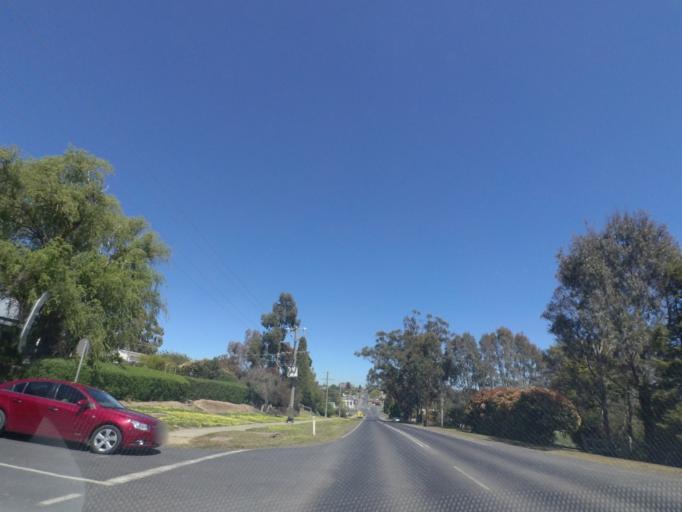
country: AU
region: Victoria
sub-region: Whittlesea
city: Whittlesea
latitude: -37.2899
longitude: 144.9544
